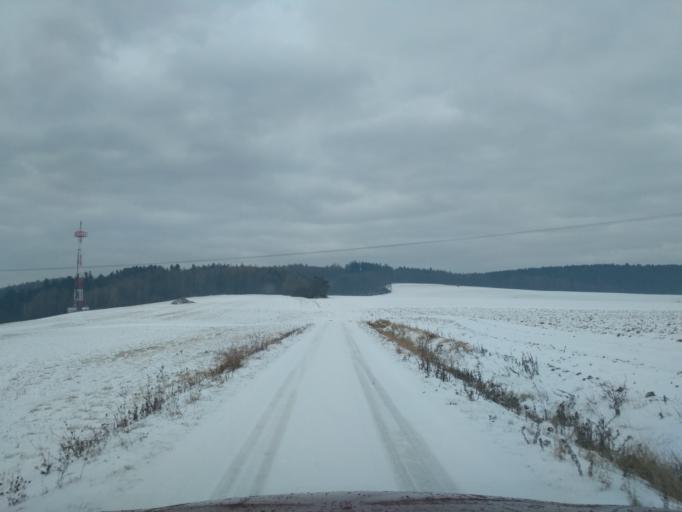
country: SK
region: Presovsky
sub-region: Okres Presov
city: Presov
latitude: 49.0037
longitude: 21.1526
